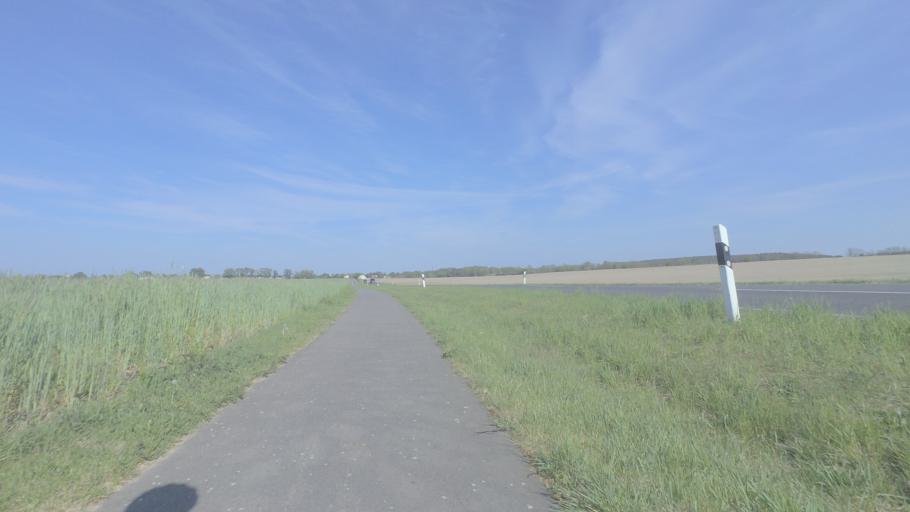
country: DE
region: Brandenburg
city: Rangsdorf
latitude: 52.2459
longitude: 13.3678
